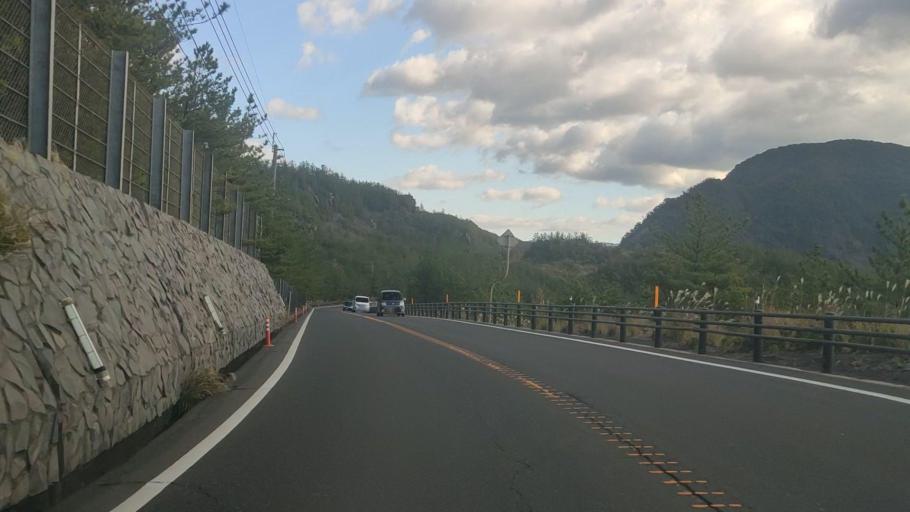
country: JP
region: Kagoshima
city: Tarumizu
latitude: 31.5536
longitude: 130.6869
